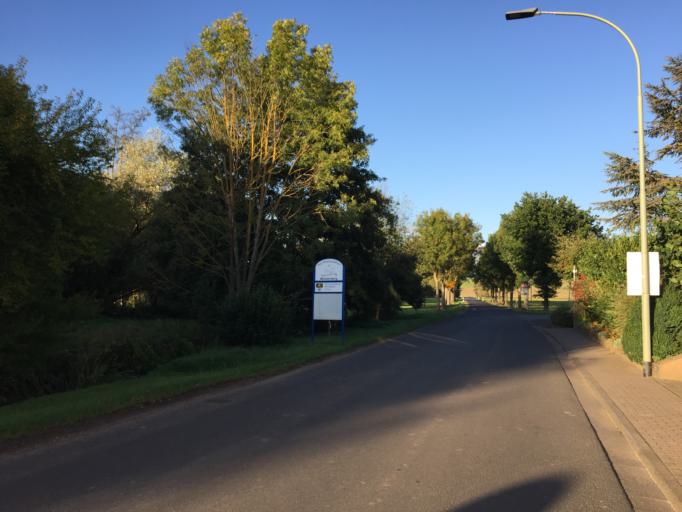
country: DE
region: Hesse
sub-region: Regierungsbezirk Darmstadt
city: Munzenberg
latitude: 50.4667
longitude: 8.7915
